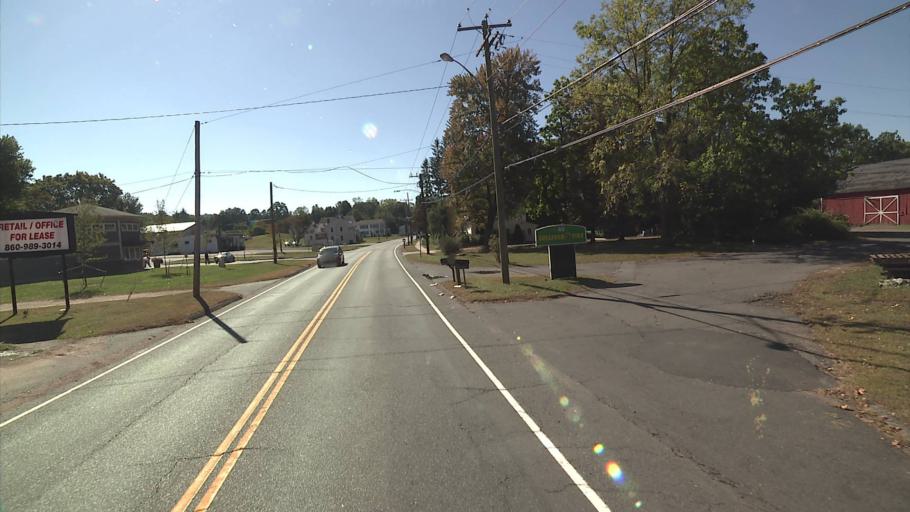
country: US
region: Connecticut
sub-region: Tolland County
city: Rockville
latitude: 41.8743
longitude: -72.4634
